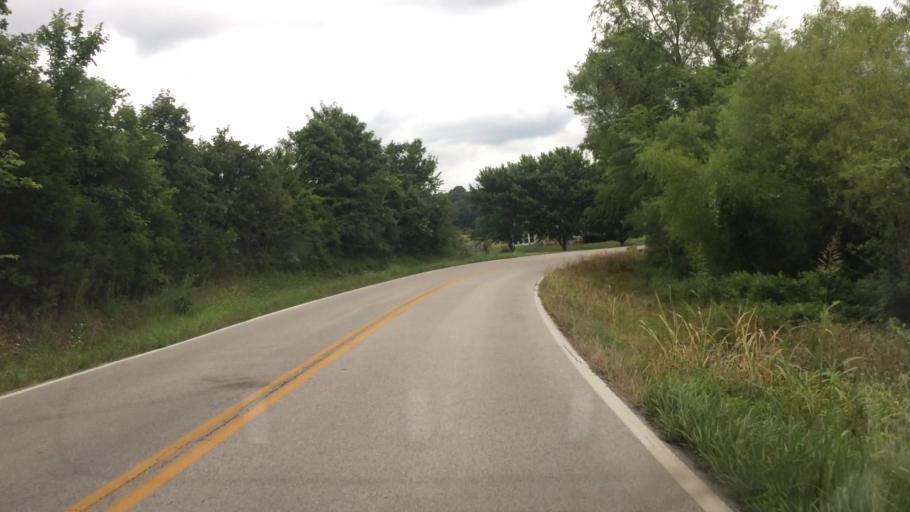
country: US
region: Missouri
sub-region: Greene County
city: Strafford
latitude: 37.2922
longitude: -93.0870
